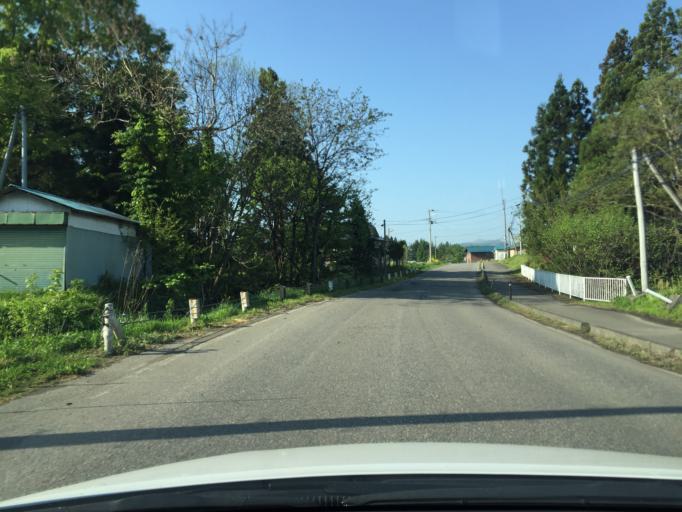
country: JP
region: Fukushima
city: Kitakata
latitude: 37.6519
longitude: 139.7752
